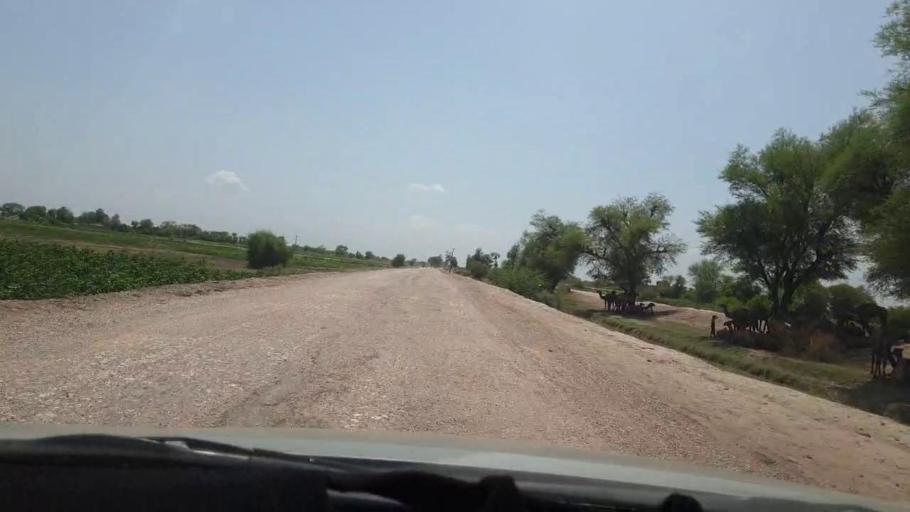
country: PK
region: Sindh
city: Pano Aqil
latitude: 27.7310
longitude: 69.1854
